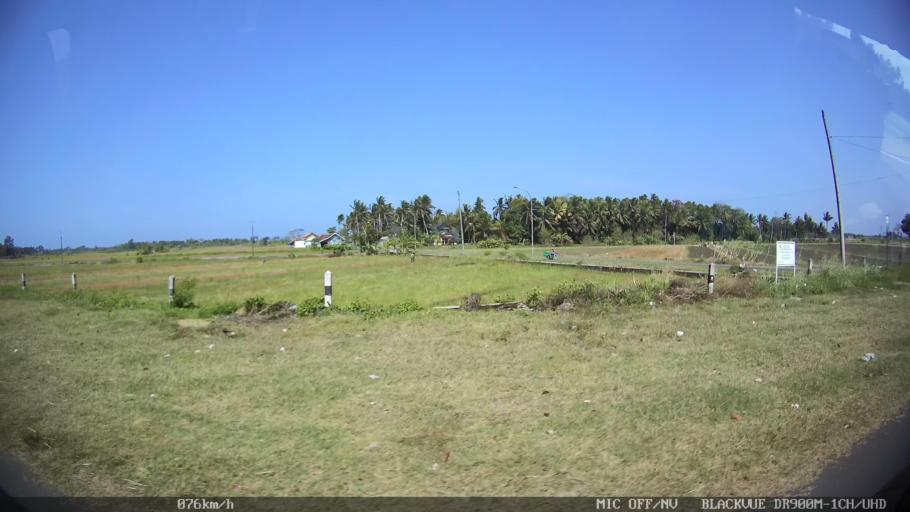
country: ID
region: Daerah Istimewa Yogyakarta
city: Srandakan
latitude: -7.9603
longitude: 110.2030
